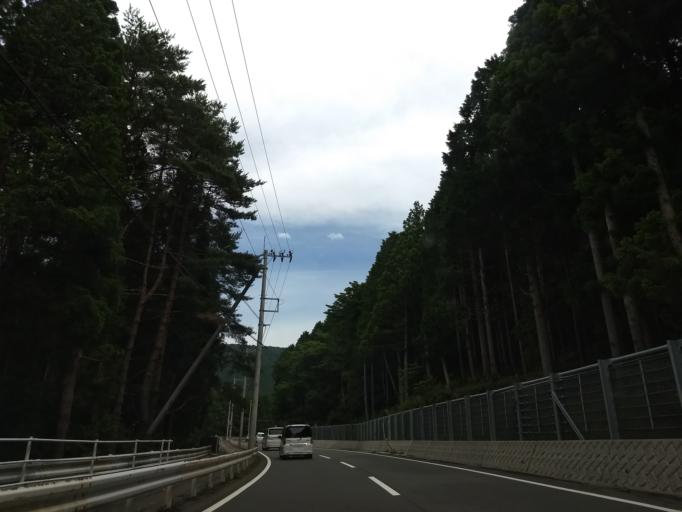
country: JP
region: Shizuoka
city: Gotemba
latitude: 35.3739
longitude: 138.8600
